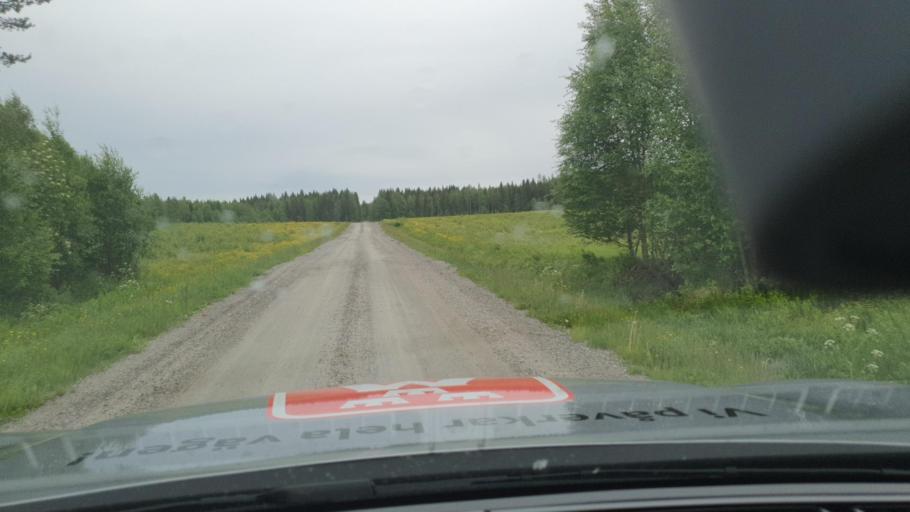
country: SE
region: Norrbotten
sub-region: Overkalix Kommun
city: OEverkalix
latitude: 66.0816
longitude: 22.9051
